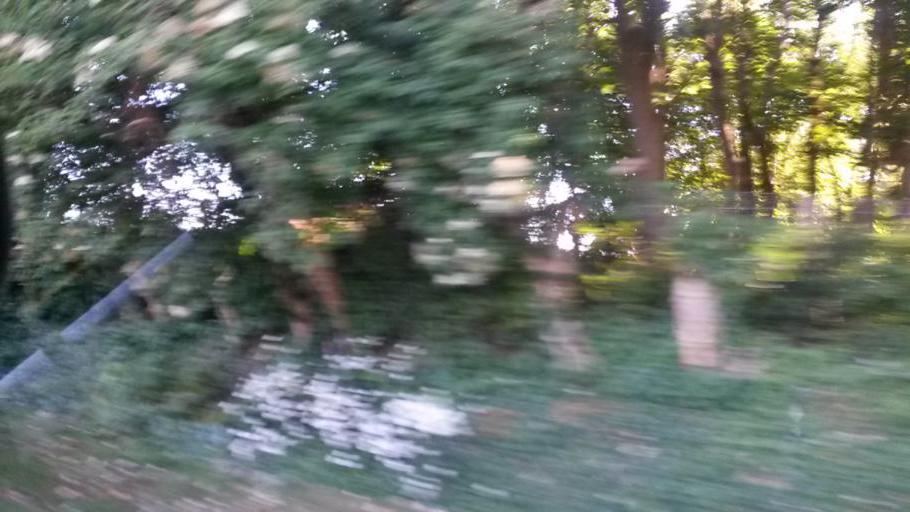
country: IE
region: Leinster
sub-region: Dublin City
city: Finglas
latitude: 53.4729
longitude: -6.3202
